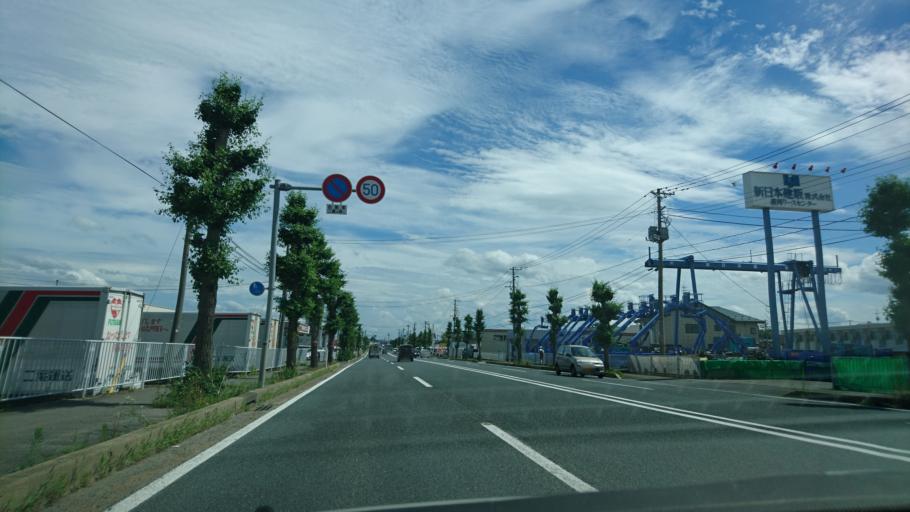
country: JP
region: Iwate
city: Morioka-shi
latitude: 39.6314
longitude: 141.1737
